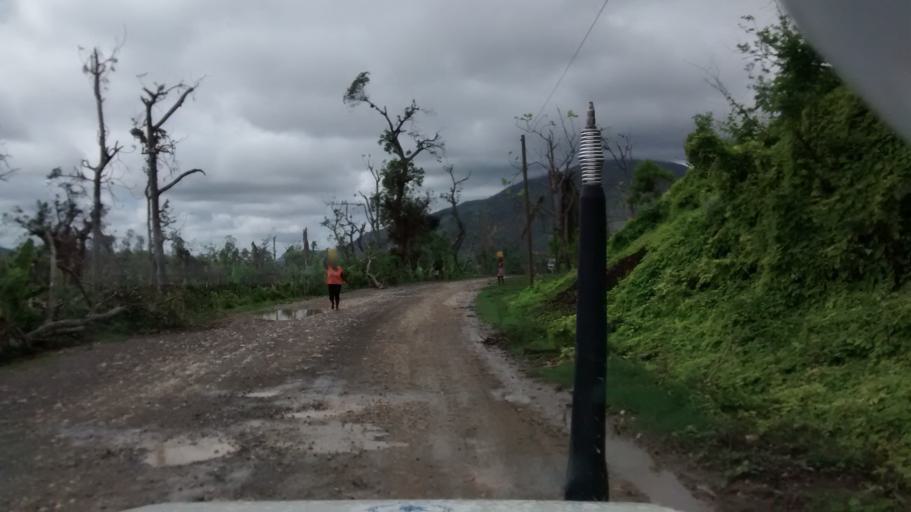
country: HT
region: Grandans
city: Moron
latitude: 18.5962
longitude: -74.1826
